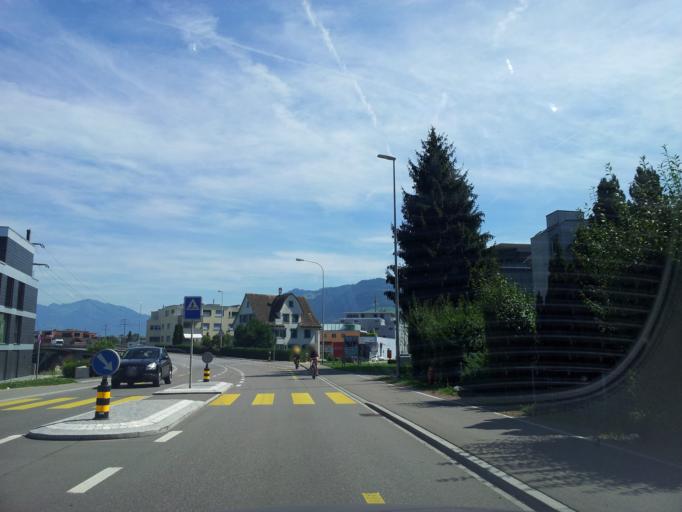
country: CH
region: Schwyz
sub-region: Bezirk March
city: Altendorf
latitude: 47.1903
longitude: 8.8373
